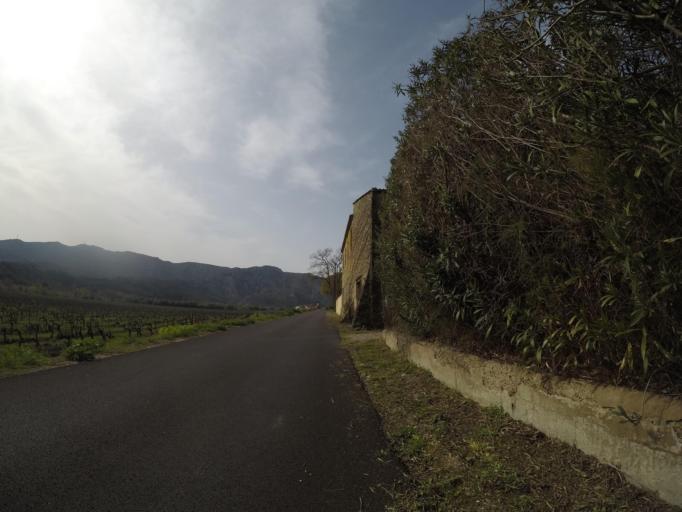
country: FR
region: Languedoc-Roussillon
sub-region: Departement des Pyrenees-Orientales
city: Baixas
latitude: 42.7830
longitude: 2.7666
